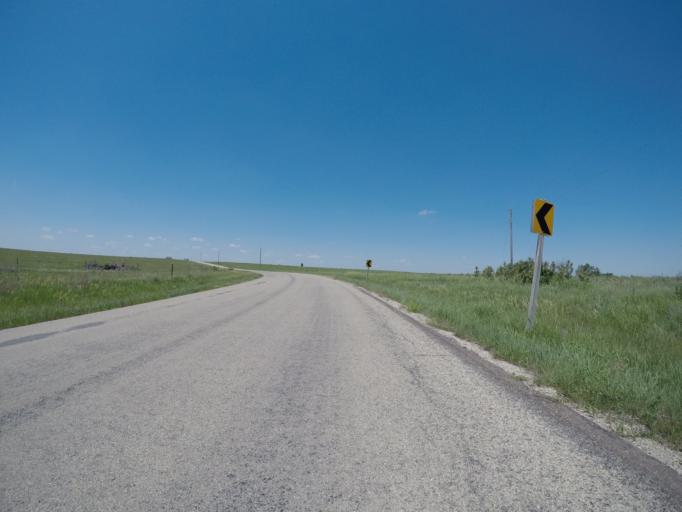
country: US
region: Kansas
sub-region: Geary County
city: Grandview Plaza
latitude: 38.8697
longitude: -96.7994
